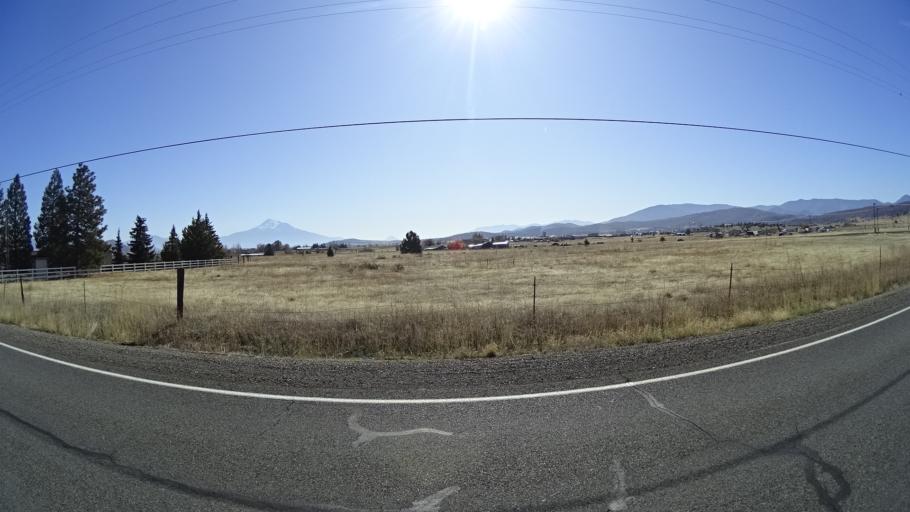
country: US
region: California
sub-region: Siskiyou County
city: Yreka
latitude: 41.7428
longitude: -122.5916
